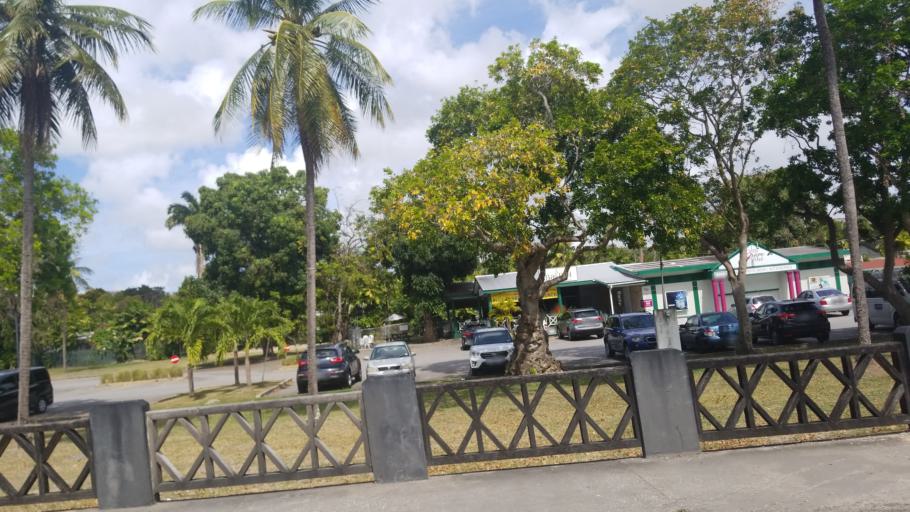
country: BB
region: Saint James
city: Holetown
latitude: 13.1824
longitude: -59.6384
